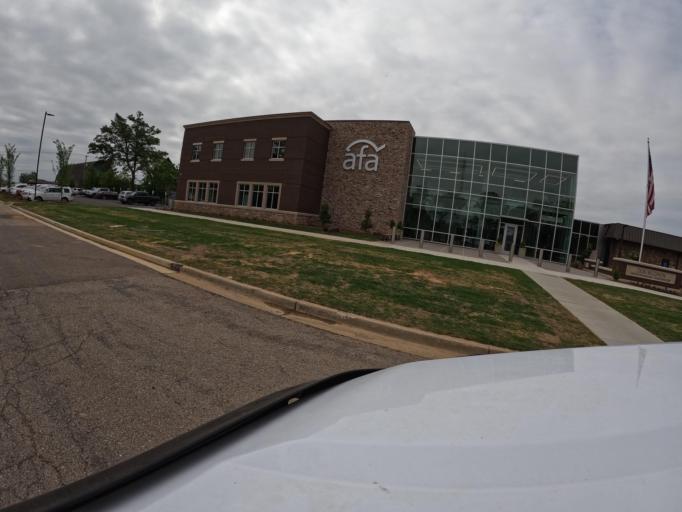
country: US
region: Mississippi
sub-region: Lee County
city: Tupelo
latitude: 34.2568
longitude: -88.7474
